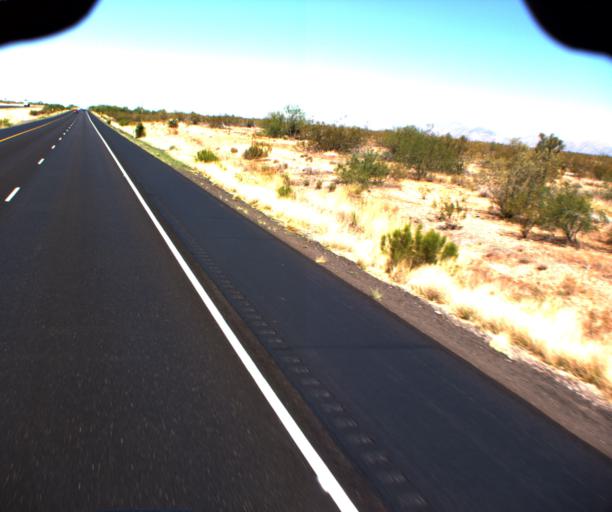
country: US
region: Arizona
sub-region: Yavapai County
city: Congress
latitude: 34.0601
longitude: -112.8595
